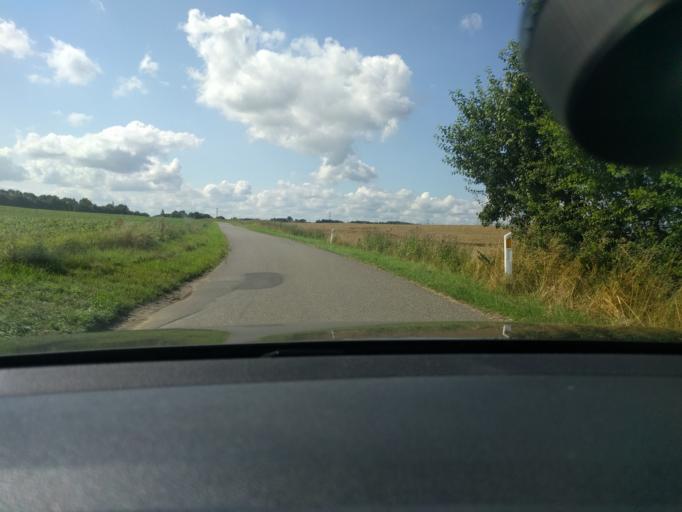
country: DK
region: Central Jutland
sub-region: Viborg Kommune
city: Viborg
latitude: 56.5071
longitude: 9.5073
